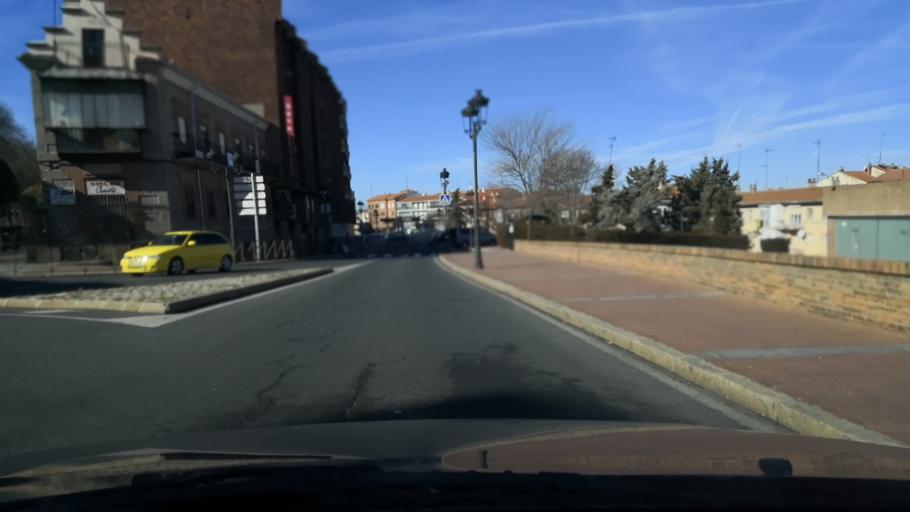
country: ES
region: Castille and Leon
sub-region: Provincia de Avila
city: Avila
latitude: 40.6572
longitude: -4.6896
